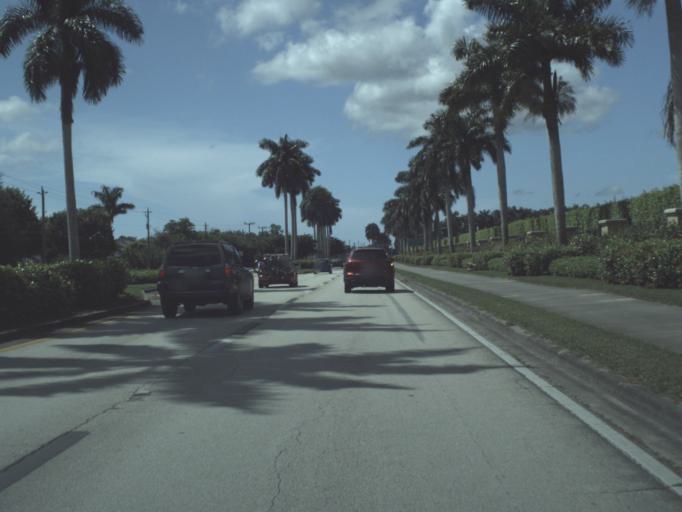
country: US
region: Florida
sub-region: Lee County
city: Harlem Heights
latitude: 26.5267
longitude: -81.9334
